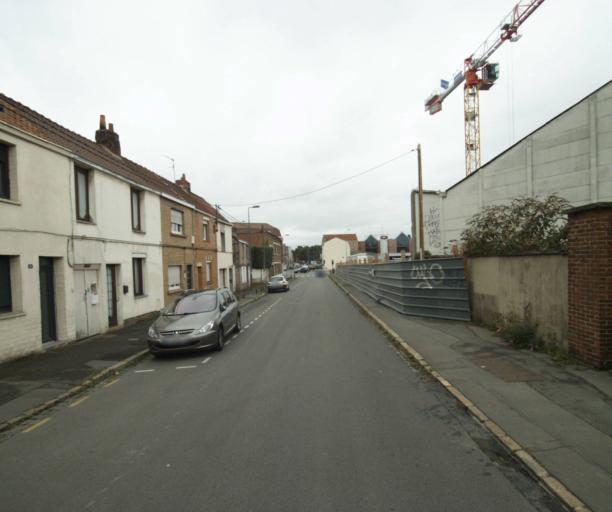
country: FR
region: Nord-Pas-de-Calais
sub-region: Departement du Nord
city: Ronchin
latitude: 50.6129
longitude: 3.0760
